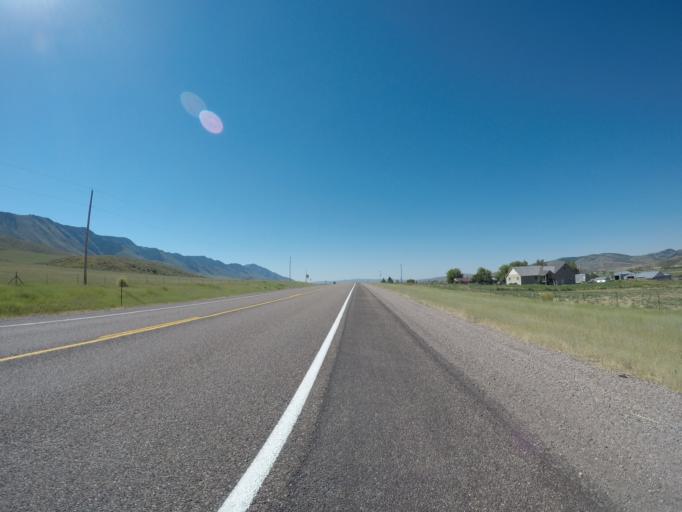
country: US
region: Idaho
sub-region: Bear Lake County
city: Montpelier
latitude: 42.3730
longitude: -111.0533
